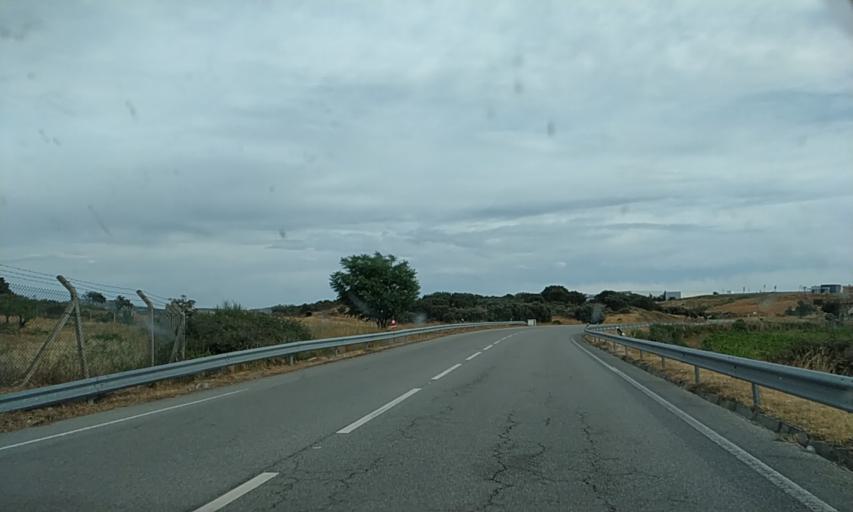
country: PT
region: Viseu
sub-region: Sao Joao da Pesqueira
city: Sao Joao da Pesqueira
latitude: 41.1222
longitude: -7.3905
